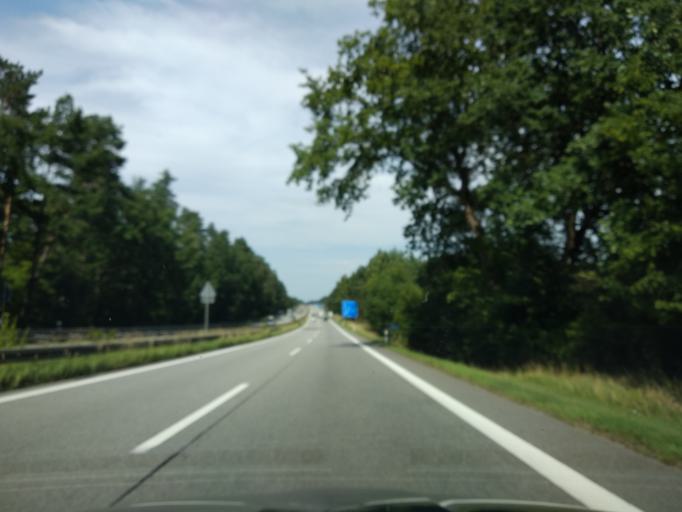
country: DE
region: Brandenburg
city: Althuttendorf
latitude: 52.9318
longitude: 13.7860
